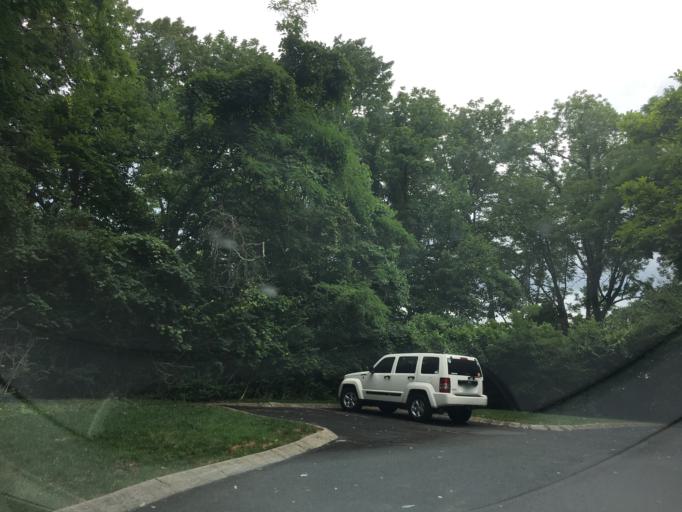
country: US
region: Tennessee
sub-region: Davidson County
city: Belle Meade
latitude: 36.0963
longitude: -86.8286
